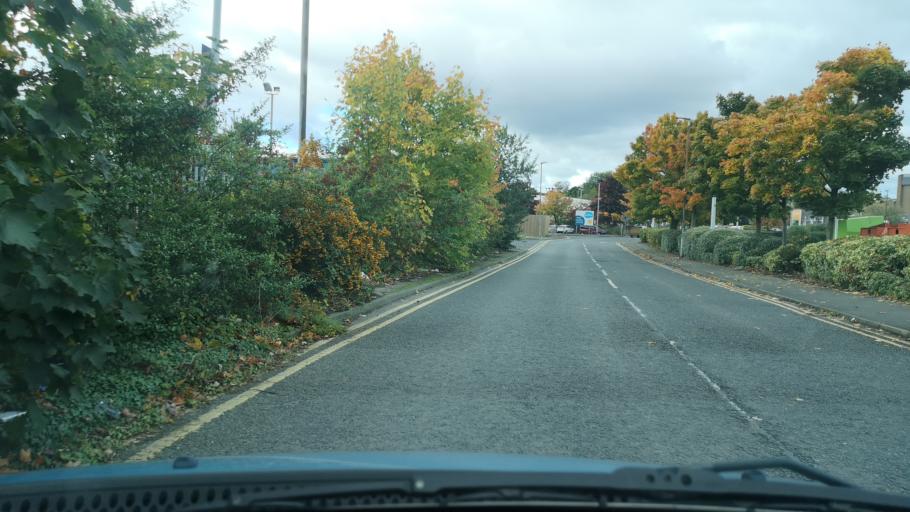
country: GB
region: England
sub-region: Kirklees
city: Dewsbury
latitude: 53.6879
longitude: -1.6241
